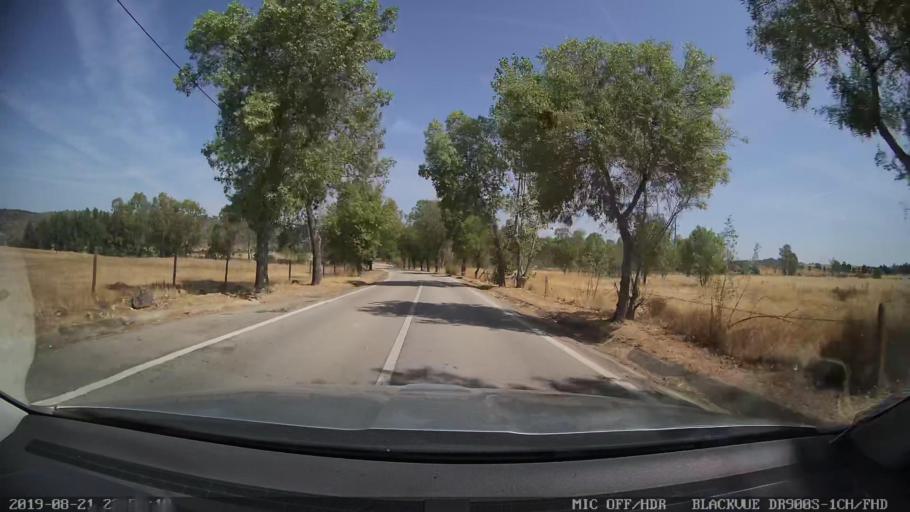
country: PT
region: Castelo Branco
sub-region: Idanha-A-Nova
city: Idanha-a-Nova
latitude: 39.8985
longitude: -7.2355
